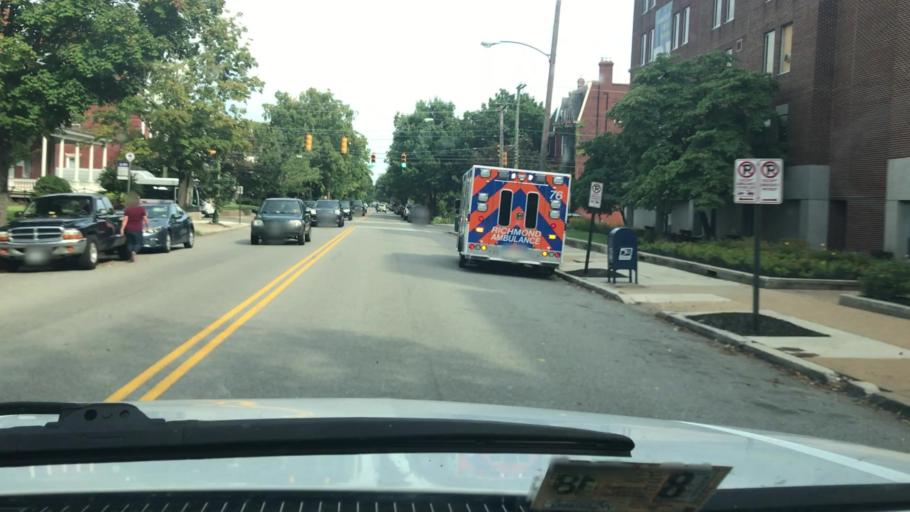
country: US
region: Virginia
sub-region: City of Richmond
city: Richmond
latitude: 37.5543
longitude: -77.4727
